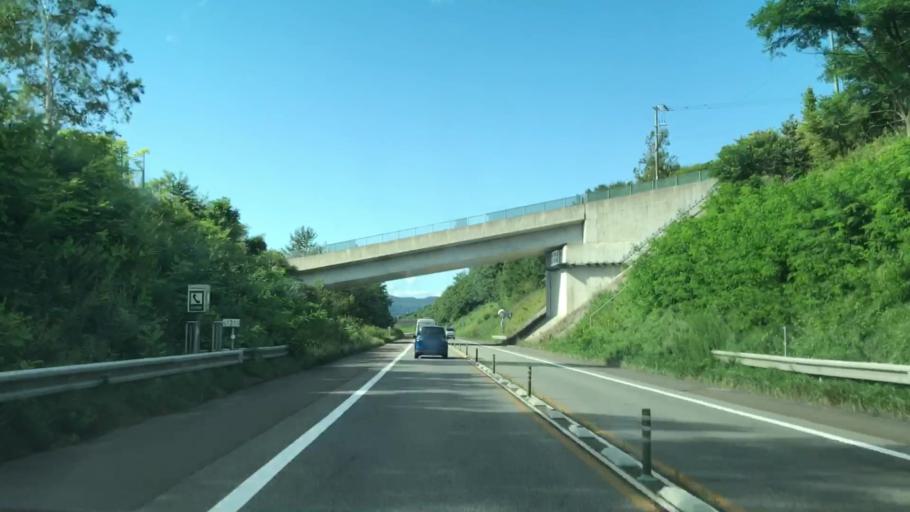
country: JP
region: Hokkaido
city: Date
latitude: 42.4725
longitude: 140.9048
